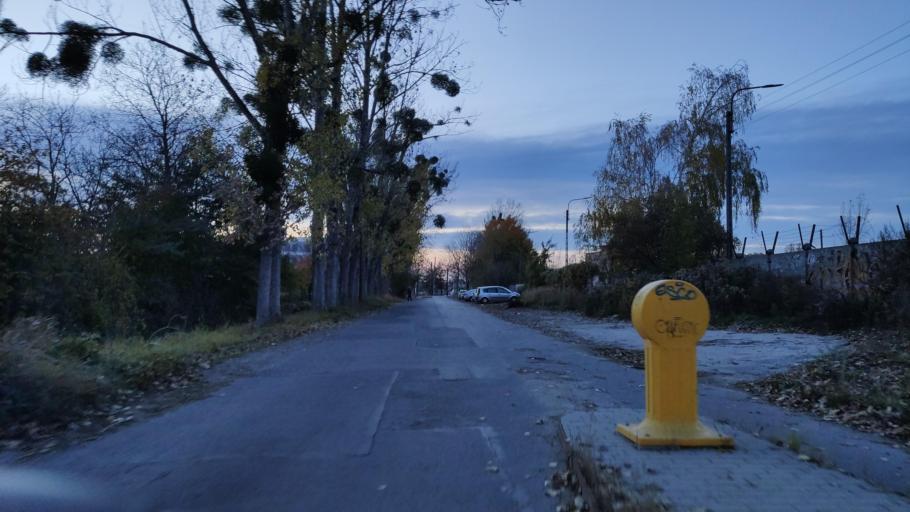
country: PL
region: Lower Silesian Voivodeship
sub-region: Powiat wroclawski
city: Zerniki Wroclawskie
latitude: 51.0688
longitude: 17.0583
